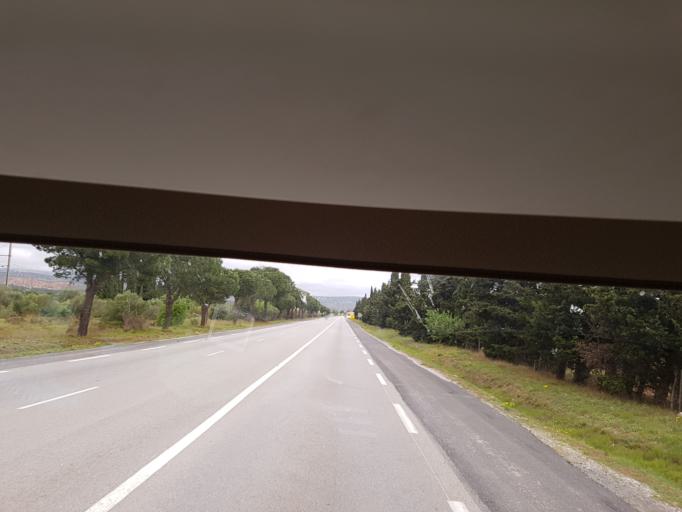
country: FR
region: Languedoc-Roussillon
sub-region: Departement des Pyrenees-Orientales
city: Salses-le-Chateau
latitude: 42.8179
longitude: 2.9153
